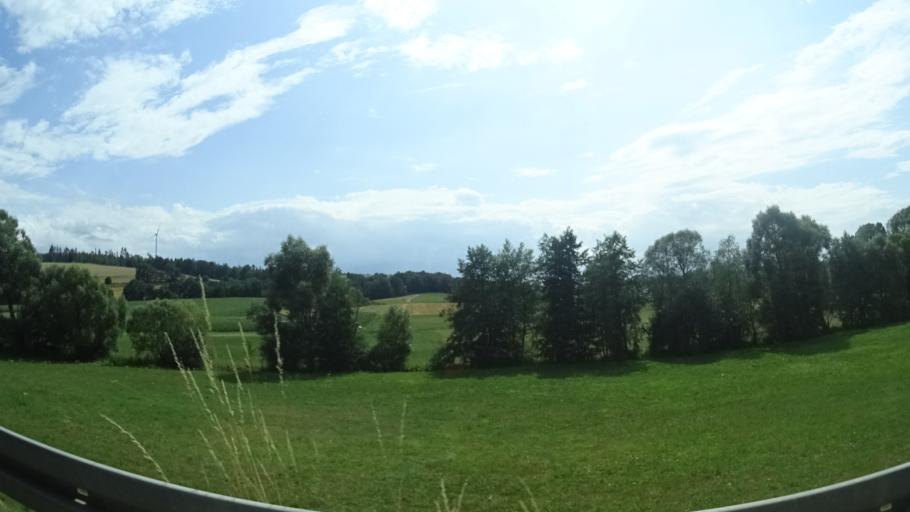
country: DE
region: Hesse
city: Grebenau
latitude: 50.7550
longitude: 9.4935
